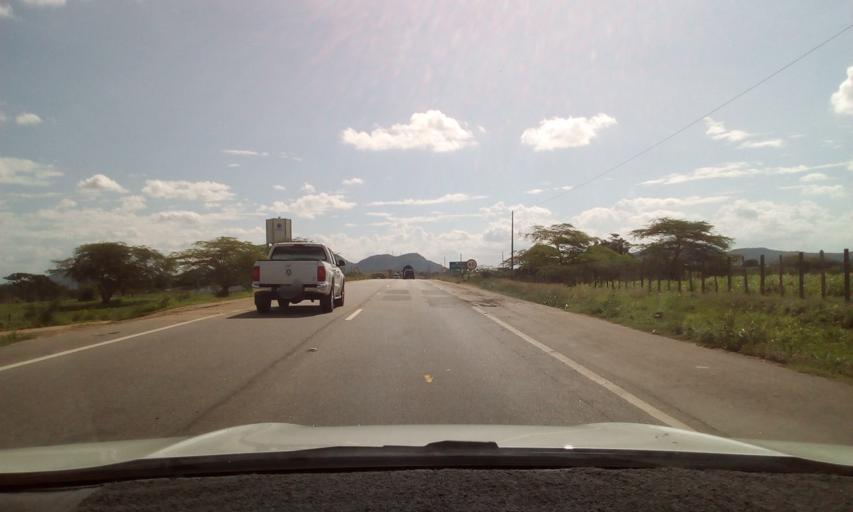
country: BR
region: Paraiba
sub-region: Gurinhem
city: Gurinhem
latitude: -7.1648
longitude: -35.3523
